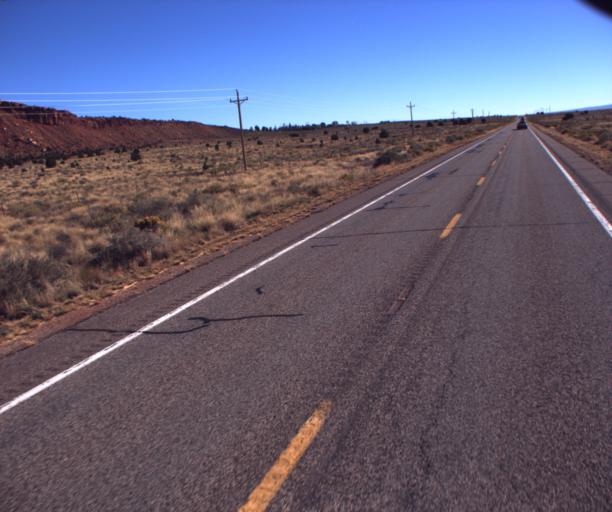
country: US
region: Arizona
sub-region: Coconino County
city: Fredonia
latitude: 36.8578
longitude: -112.7553
